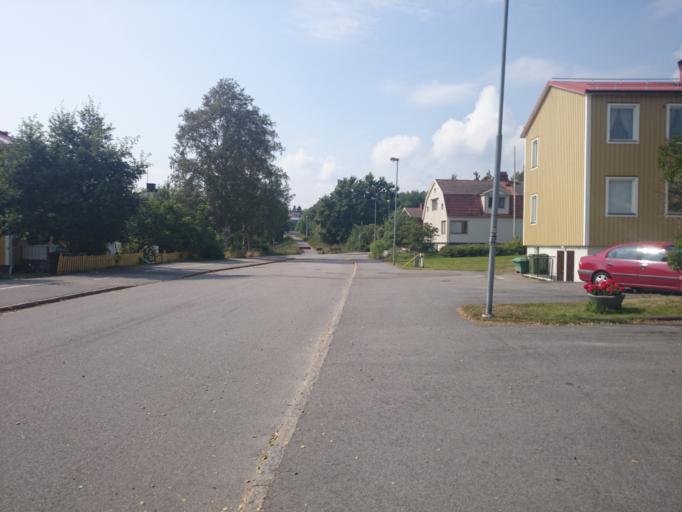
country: SE
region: Vaesternorrland
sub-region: Haernoesands Kommun
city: Haernoesand
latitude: 62.6391
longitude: 17.9239
